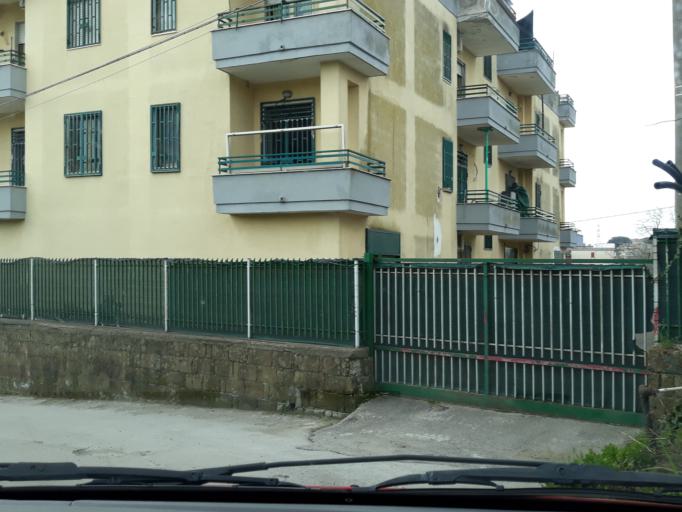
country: IT
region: Campania
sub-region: Provincia di Napoli
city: Mugnano di Napoli
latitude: 40.8838
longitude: 14.2252
